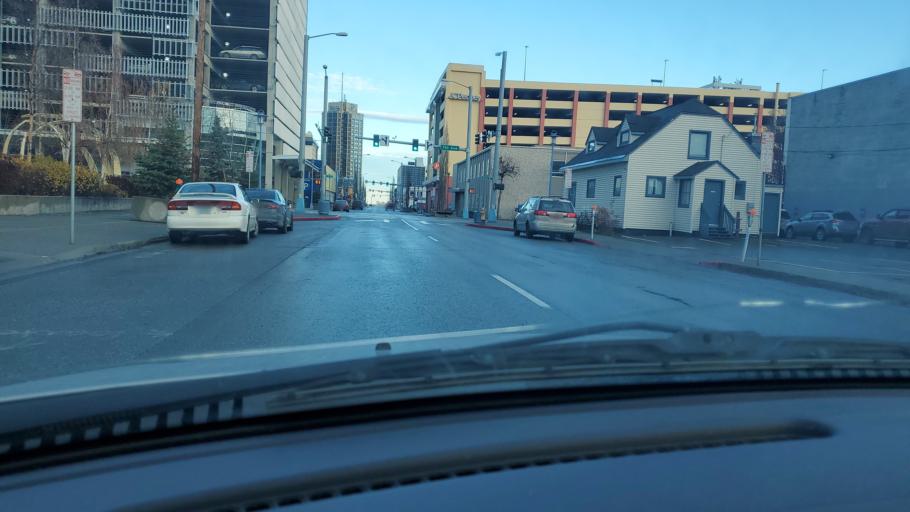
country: US
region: Alaska
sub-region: Anchorage Municipality
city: Anchorage
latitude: 61.2151
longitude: -149.8915
